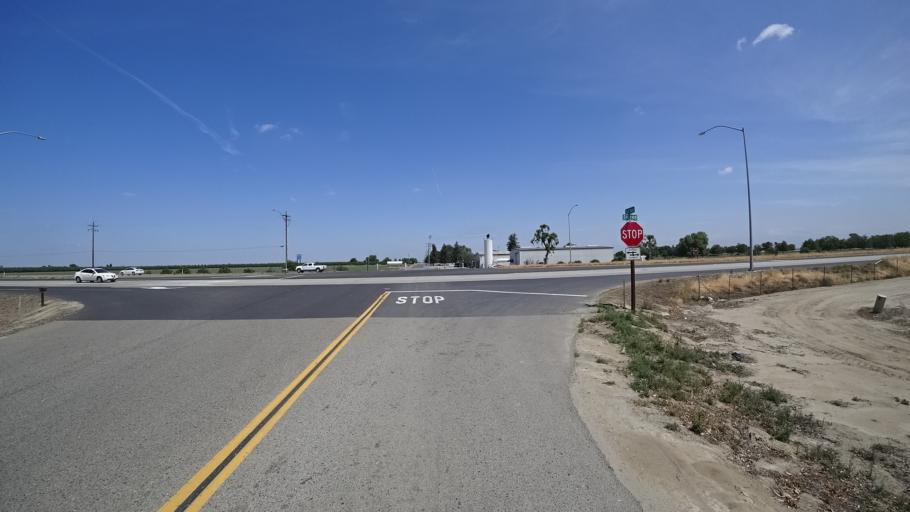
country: US
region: California
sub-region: Tulare County
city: Goshen
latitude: 36.3275
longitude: -119.4754
